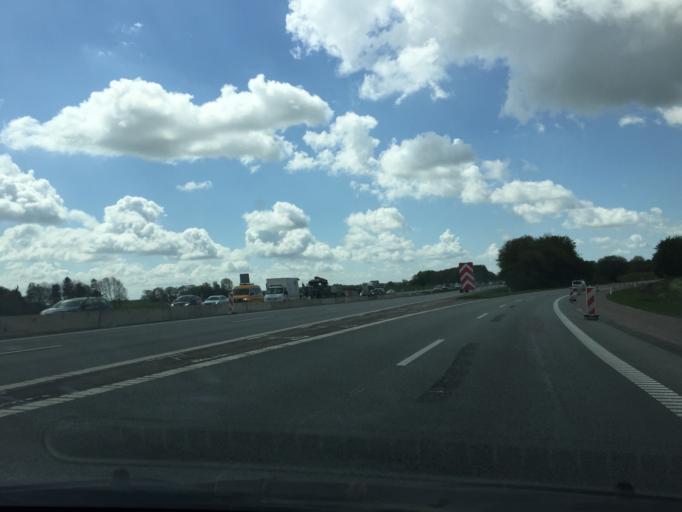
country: DK
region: Zealand
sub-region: Koge Kommune
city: Koge
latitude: 55.4800
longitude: 12.1464
